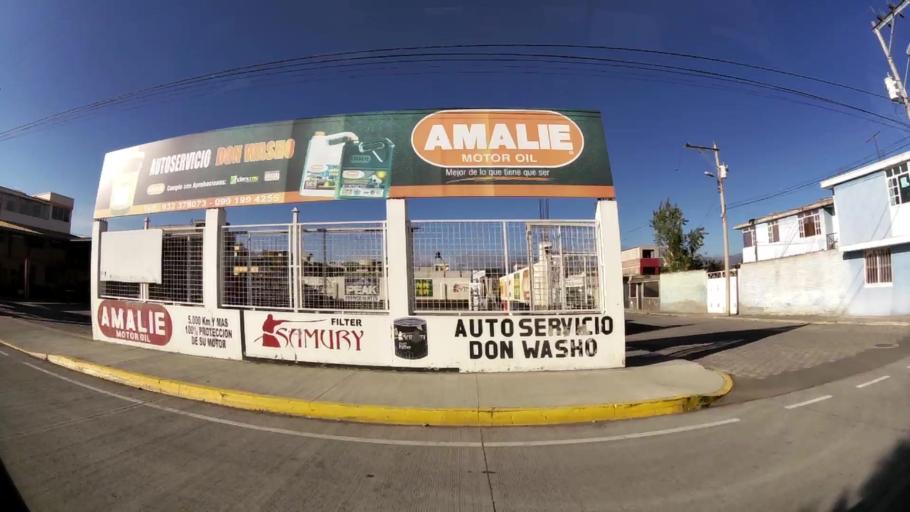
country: EC
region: Chimborazo
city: Riobamba
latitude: -1.6750
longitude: -78.6312
